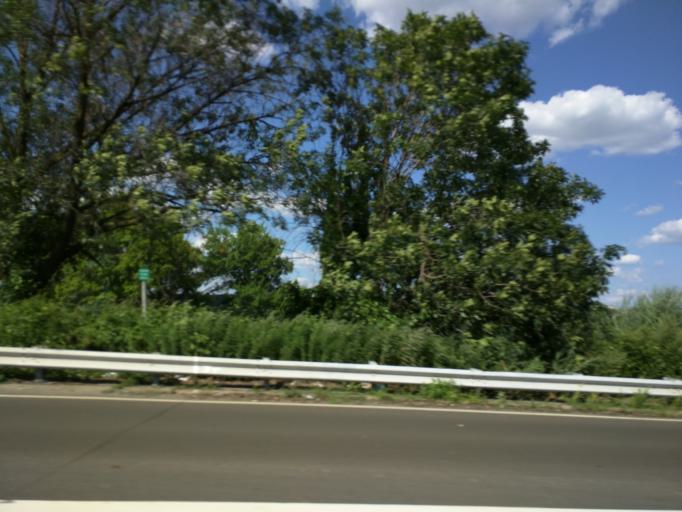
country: US
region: New York
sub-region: Queens County
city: Borough of Queens
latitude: 40.7316
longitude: -73.8421
